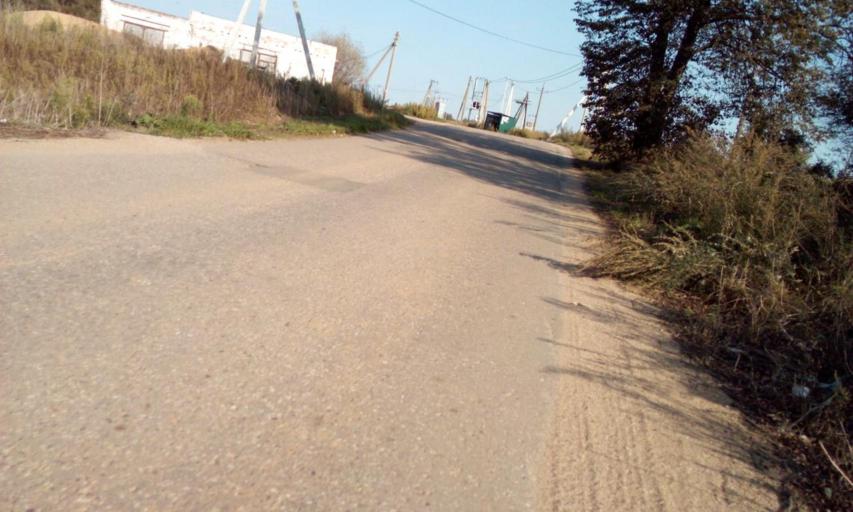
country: RU
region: Moskovskaya
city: Kolyubakino
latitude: 55.6401
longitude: 36.5444
